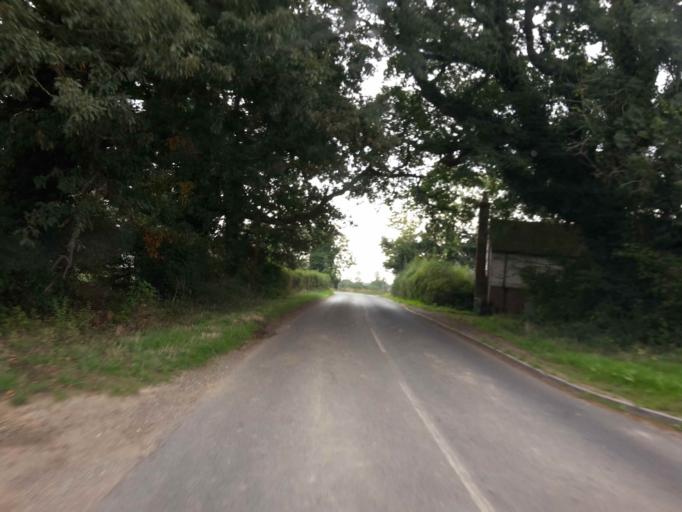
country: GB
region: England
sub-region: West Sussex
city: Billingshurst
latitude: 51.0502
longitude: -0.4325
